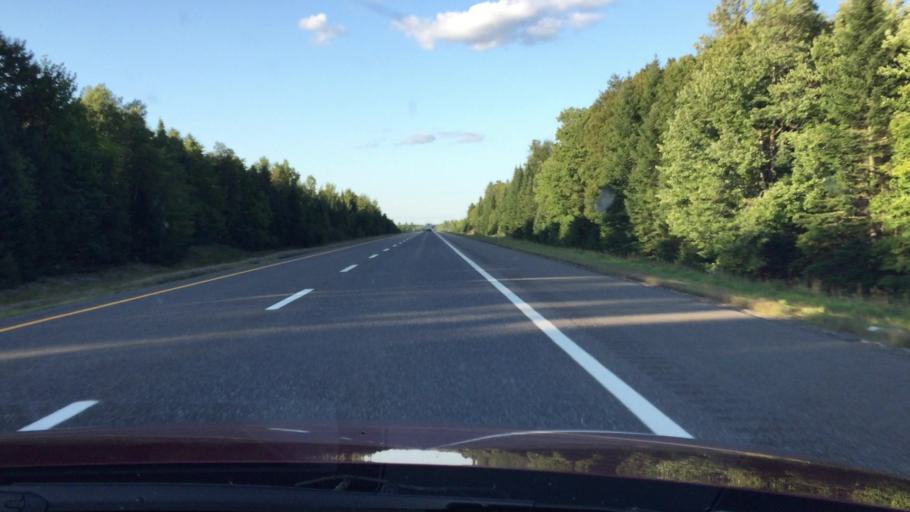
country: US
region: Maine
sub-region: Penobscot County
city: Patten
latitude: 46.0571
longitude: -68.2364
